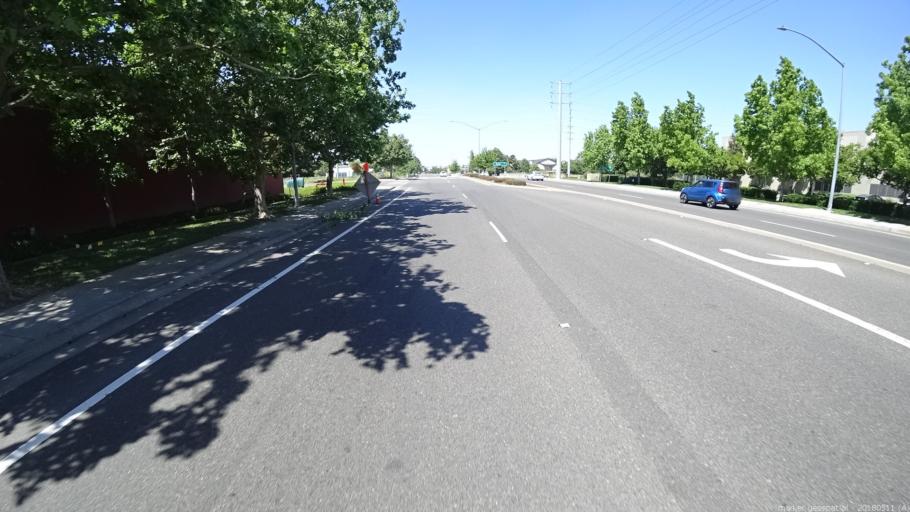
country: US
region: California
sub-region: Sacramento County
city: Sacramento
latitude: 38.6468
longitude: -121.5060
